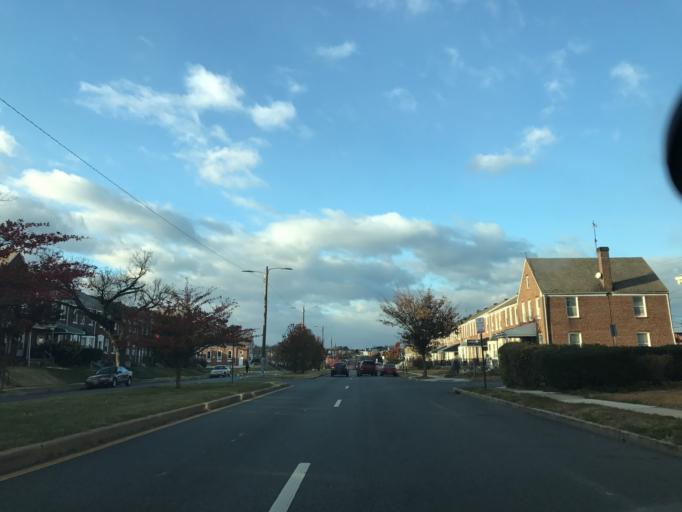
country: US
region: Maryland
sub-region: City of Baltimore
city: Baltimore
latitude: 39.3175
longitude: -76.5698
